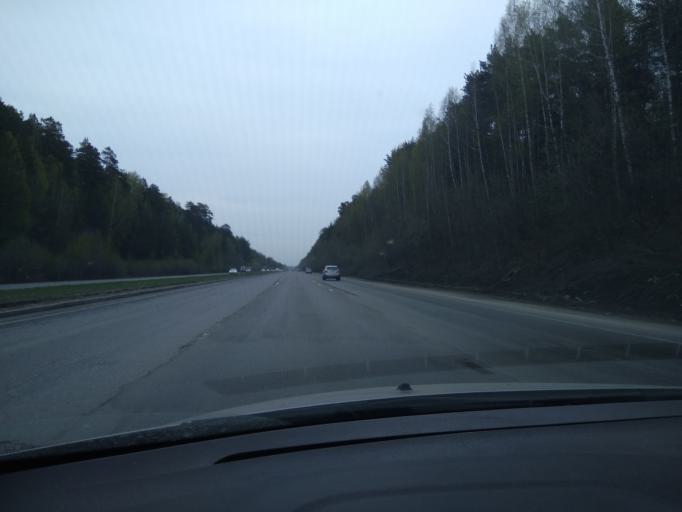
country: RU
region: Sverdlovsk
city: Istok
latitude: 56.8157
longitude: 60.7377
